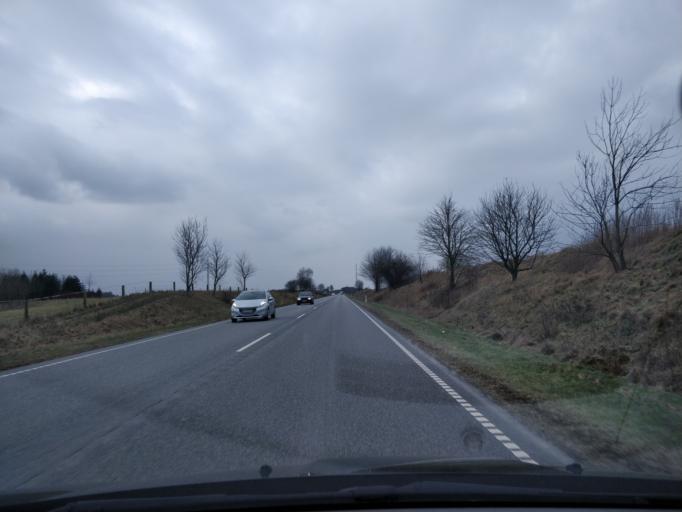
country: DK
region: South Denmark
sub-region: Vejle Kommune
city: Brejning
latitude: 55.6273
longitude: 9.7167
